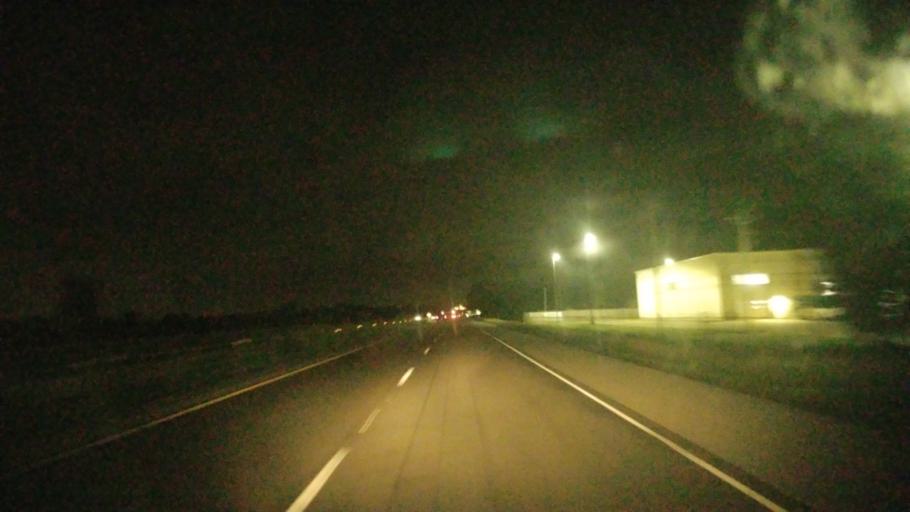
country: US
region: Illinois
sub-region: Madison County
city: Mitchell
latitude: 38.7578
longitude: -90.0751
